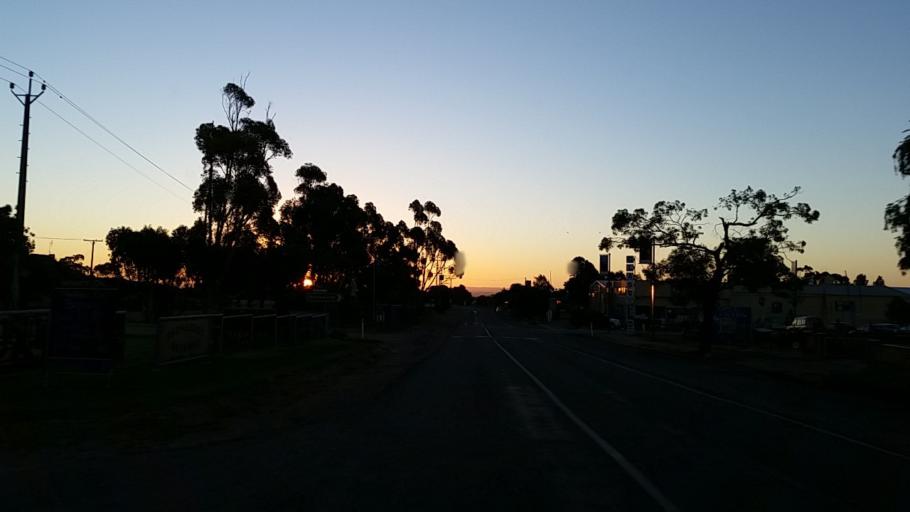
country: AU
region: South Australia
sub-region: Clare and Gilbert Valleys
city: Clare
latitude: -33.8477
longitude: 138.4899
